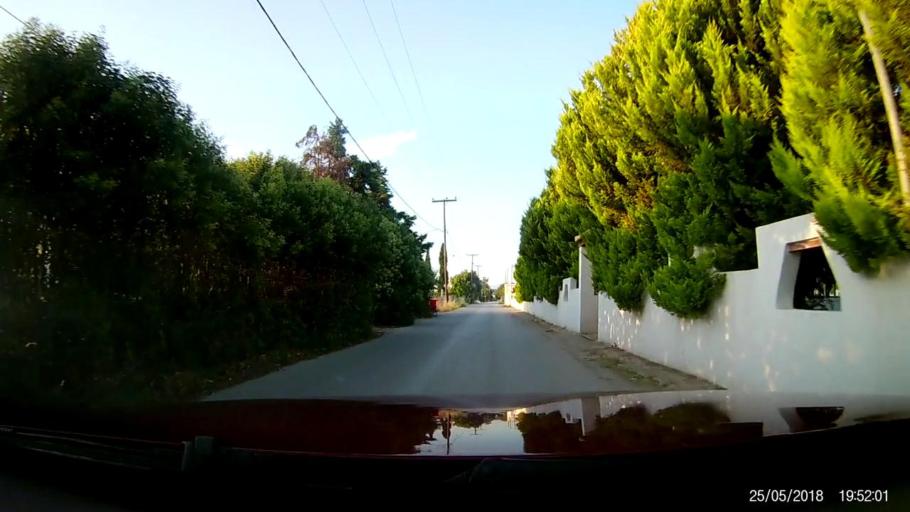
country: GR
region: Central Greece
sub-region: Nomos Evvoias
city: Ayios Nikolaos
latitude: 38.4084
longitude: 23.6432
